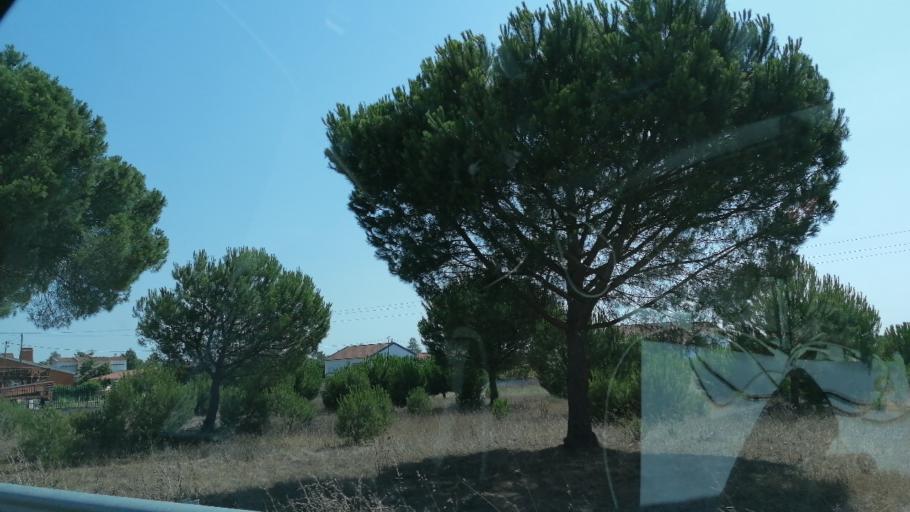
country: PT
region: Santarem
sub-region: Benavente
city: Poceirao
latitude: 38.7474
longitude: -8.6647
